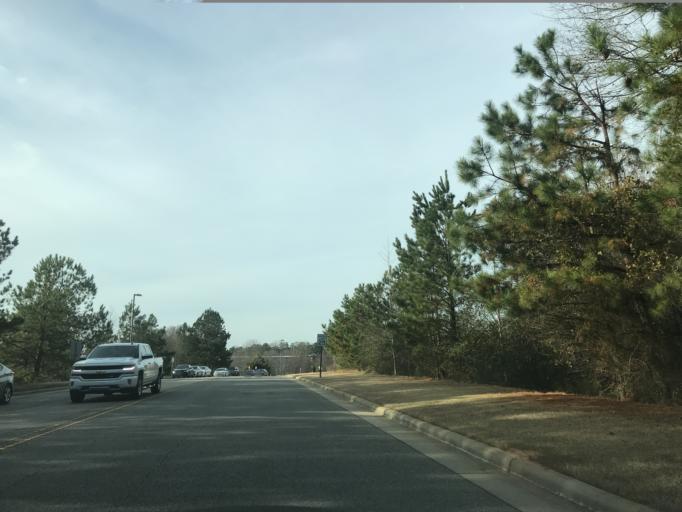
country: US
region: North Carolina
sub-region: Wake County
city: West Raleigh
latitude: 35.7671
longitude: -78.6763
